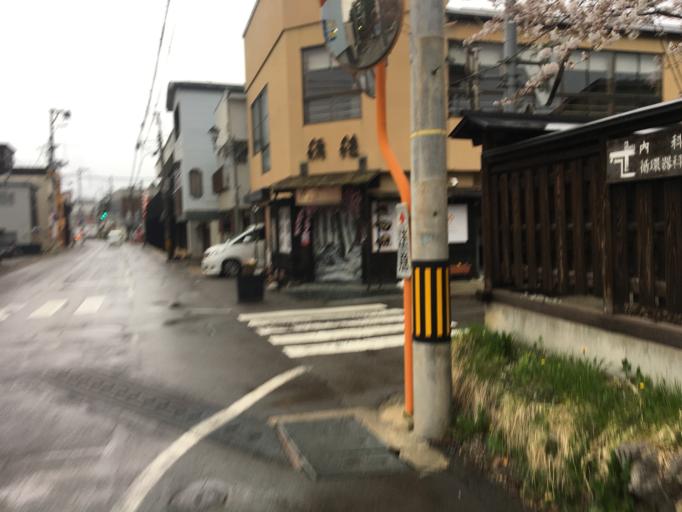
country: JP
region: Akita
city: Kakunodatemachi
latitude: 39.5937
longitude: 140.5653
